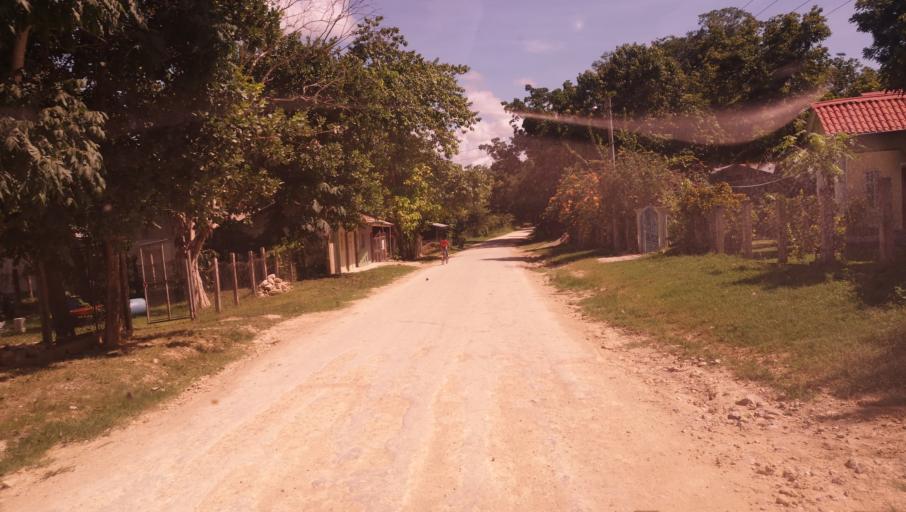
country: GT
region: Peten
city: Melchor de Mencos
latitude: 16.9758
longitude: -89.2632
